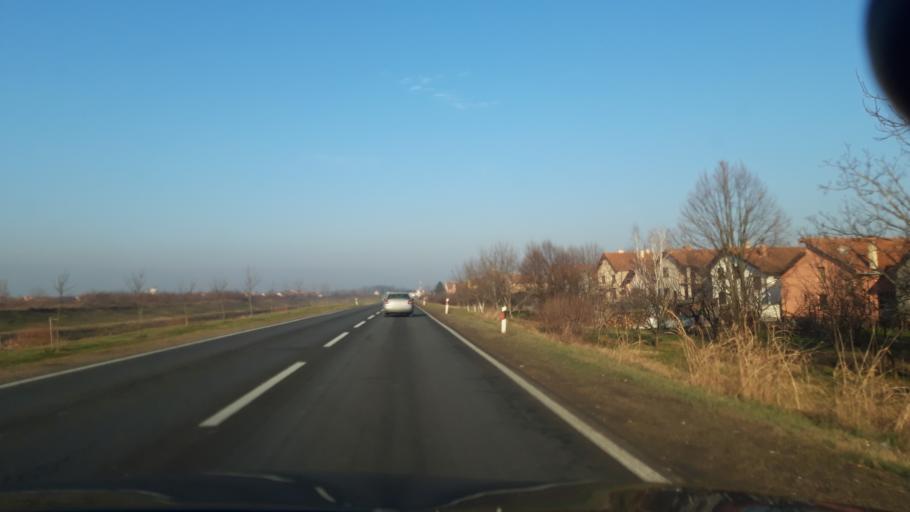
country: RS
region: Central Serbia
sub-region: Macvanski Okrug
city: Sabac
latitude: 44.7435
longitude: 19.6707
